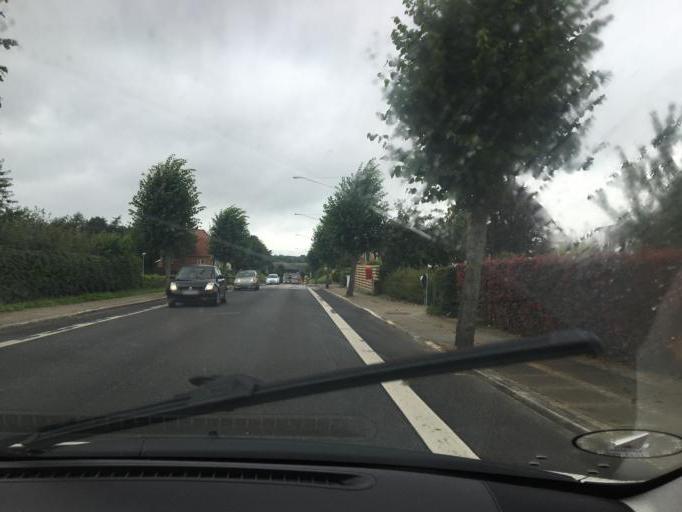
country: DK
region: South Denmark
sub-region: Middelfart Kommune
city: Middelfart
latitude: 55.4945
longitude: 9.7542
